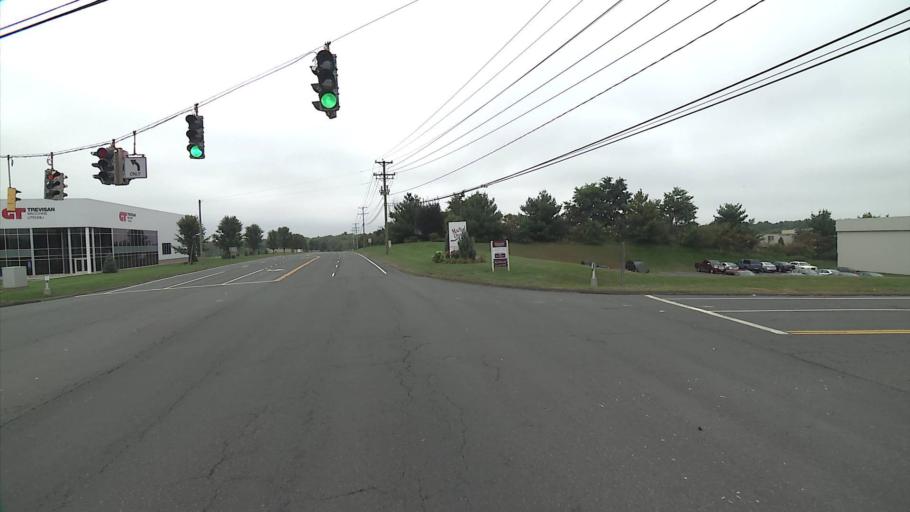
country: US
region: Connecticut
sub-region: Hartford County
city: Suffield Depot
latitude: 41.9625
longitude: -72.6626
